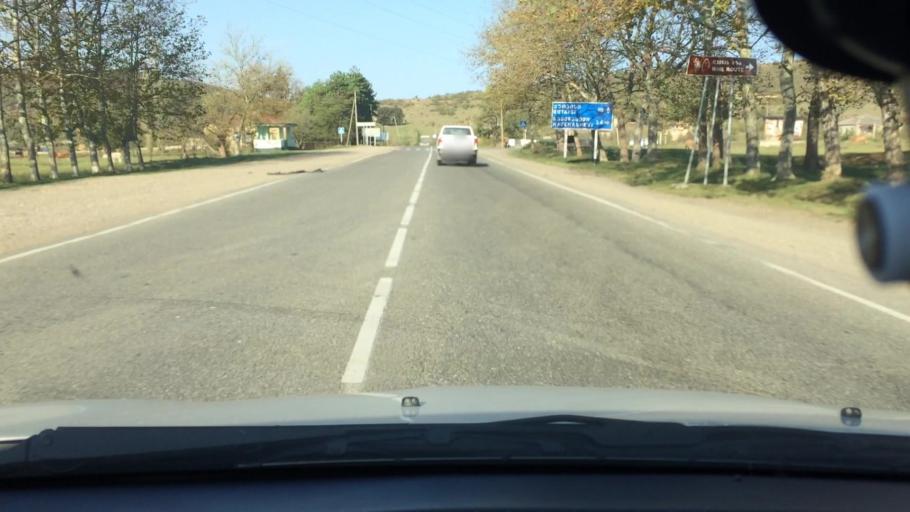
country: GE
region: Imereti
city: Kutaisi
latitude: 42.2149
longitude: 42.8127
